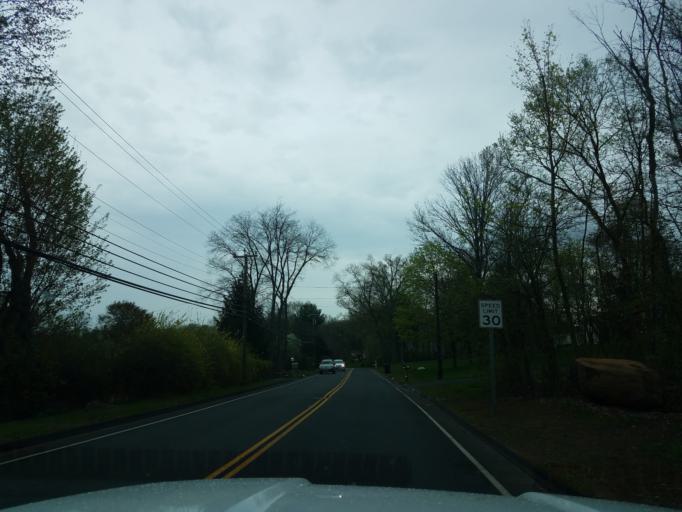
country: US
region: Connecticut
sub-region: Hartford County
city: Farmington
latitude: 41.7222
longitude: -72.7843
